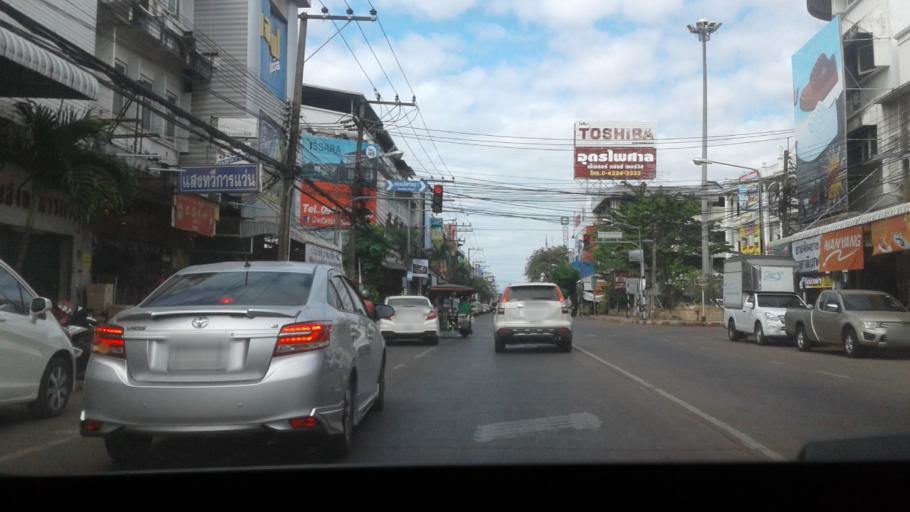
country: TH
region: Changwat Udon Thani
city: Udon Thani
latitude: 17.4060
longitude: 102.7907
